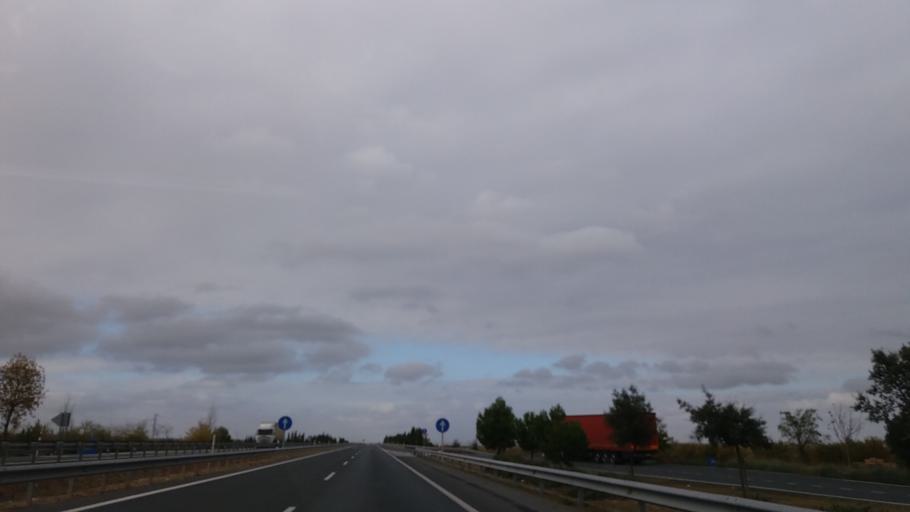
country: ES
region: Navarre
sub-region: Provincia de Navarra
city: Bunuel
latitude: 41.9402
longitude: -1.4697
